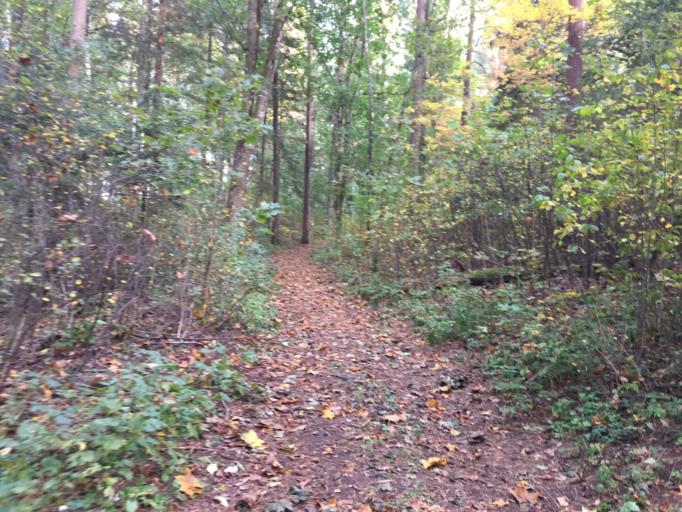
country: LV
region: Garkalne
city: Garkalne
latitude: 56.9684
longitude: 24.4957
